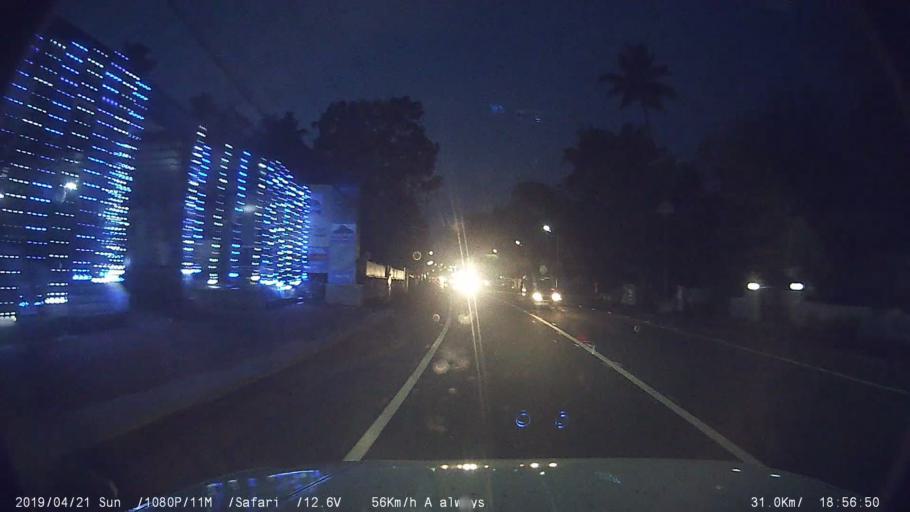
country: IN
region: Kerala
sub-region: Kottayam
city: Kottayam
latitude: 9.6525
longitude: 76.5509
